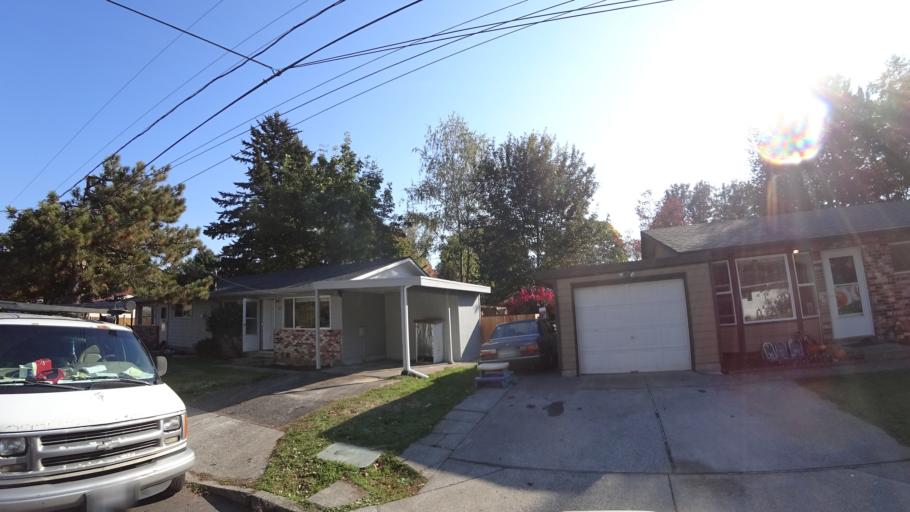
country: US
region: Oregon
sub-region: Multnomah County
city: Gresham
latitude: 45.5072
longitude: -122.4332
